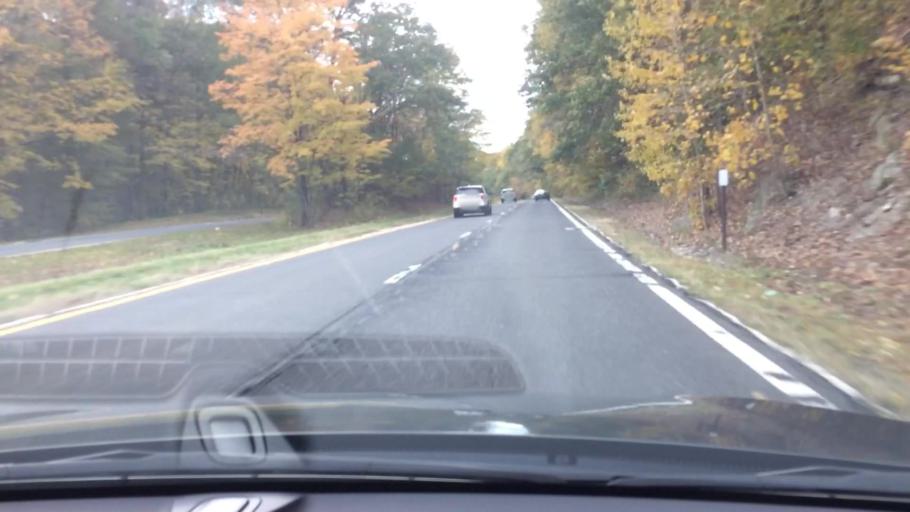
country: US
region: New York
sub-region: Dutchess County
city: Hillside Lake
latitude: 41.6817
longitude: -73.7870
